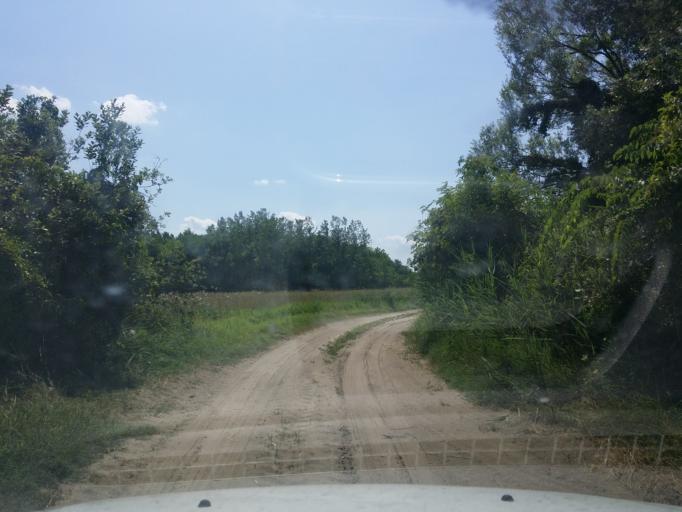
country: HU
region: Bacs-Kiskun
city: Jaszszentlaszlo
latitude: 46.6005
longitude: 19.7088
